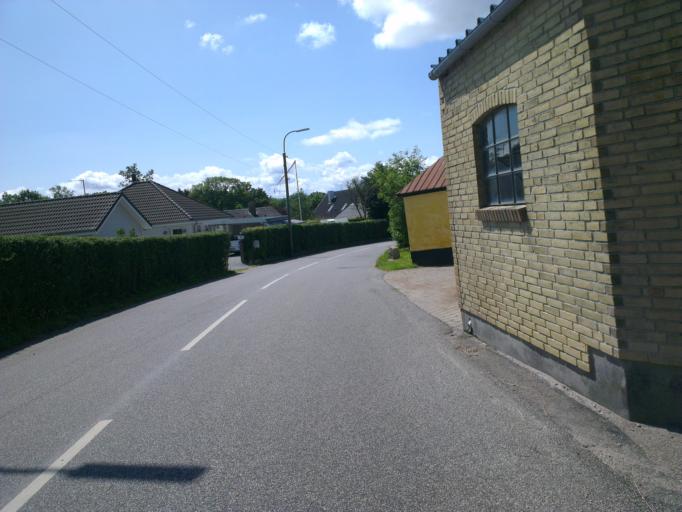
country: DK
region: Capital Region
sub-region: Frederikssund Kommune
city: Skibby
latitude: 55.7646
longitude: 11.8911
